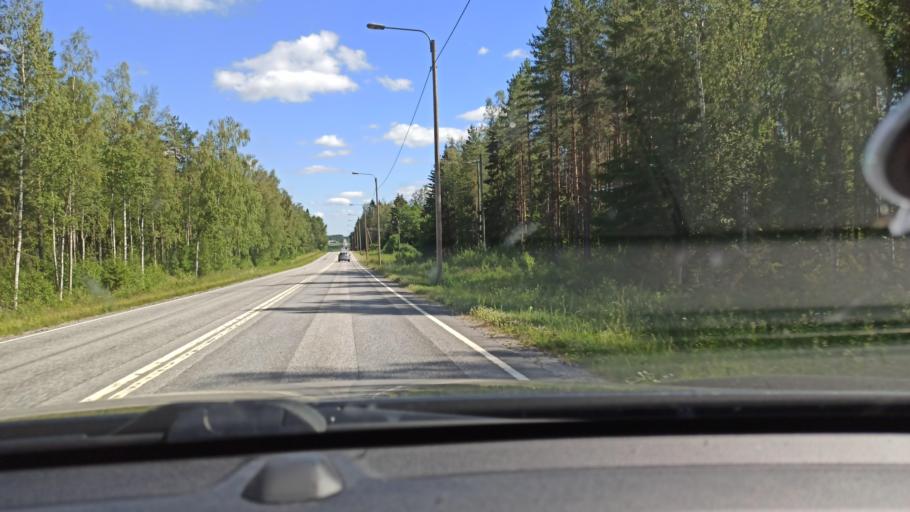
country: FI
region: Ostrobothnia
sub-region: Vaasa
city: Malax
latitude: 62.9971
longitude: 21.6619
